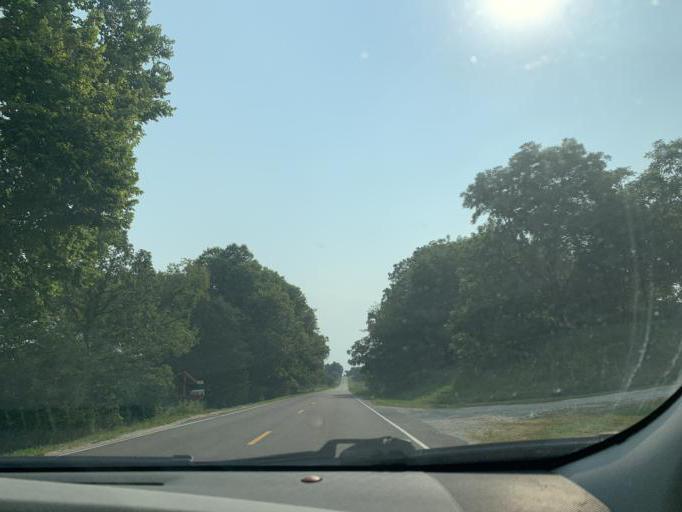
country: US
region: Illinois
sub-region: Whiteside County
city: Sterling
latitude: 41.8442
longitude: -89.7965
